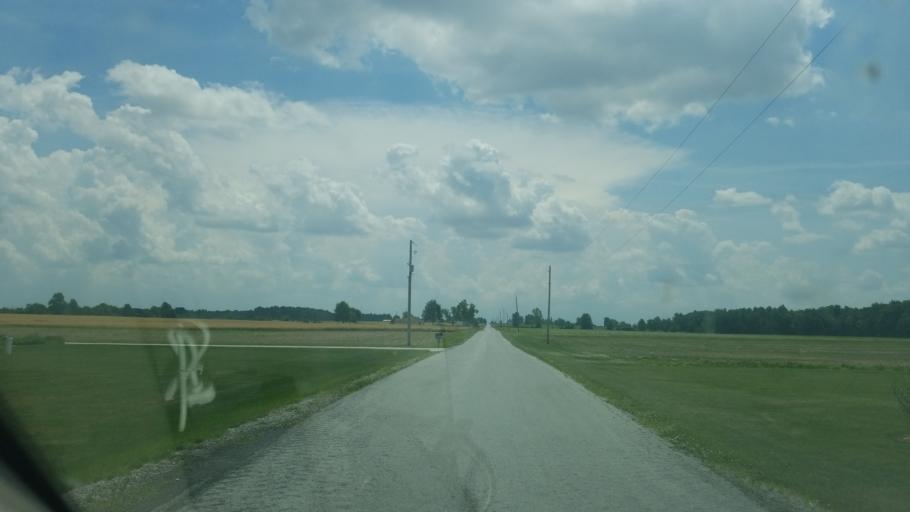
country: US
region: Ohio
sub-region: Hancock County
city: Arlington
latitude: 40.8169
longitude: -83.6050
